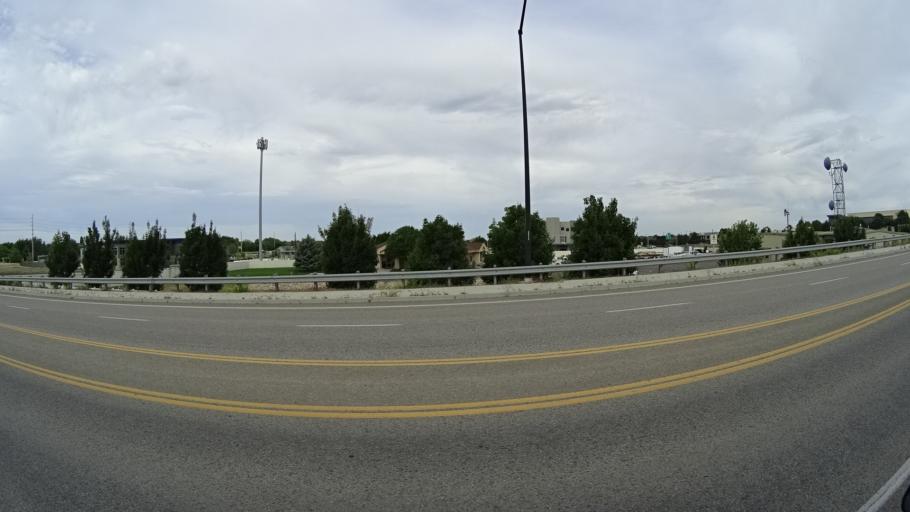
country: US
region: Idaho
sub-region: Ada County
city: Meridian
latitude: 43.5920
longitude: -116.3745
